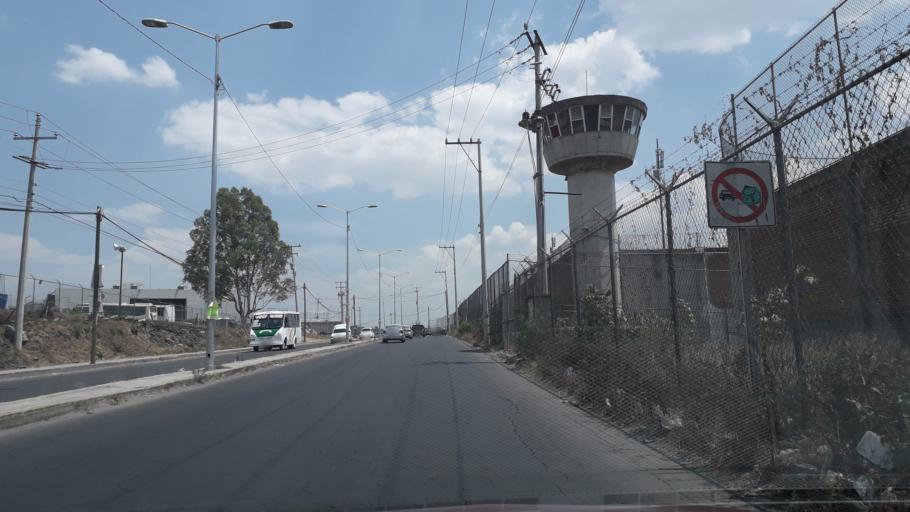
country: MX
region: Puebla
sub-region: Puebla
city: Galaxia la Calera
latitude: 18.9930
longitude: -98.1725
